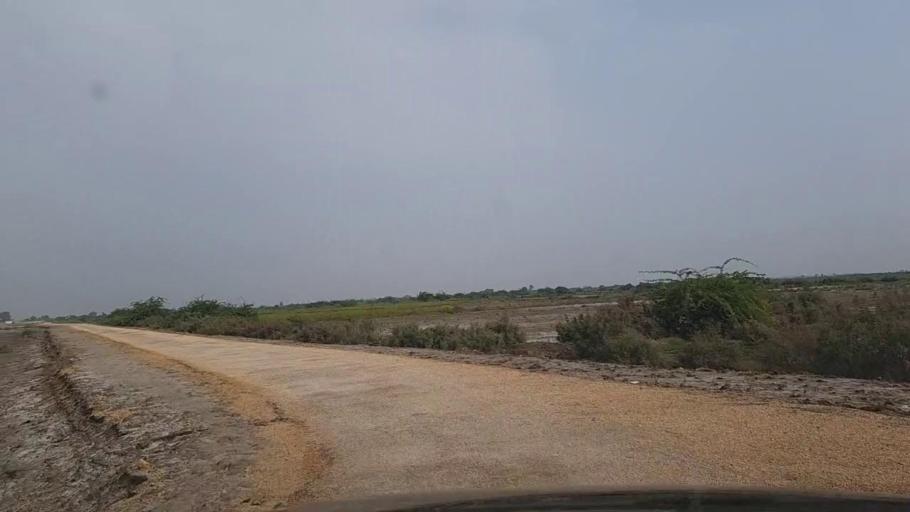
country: PK
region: Sindh
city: Thatta
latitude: 24.7456
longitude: 67.8262
